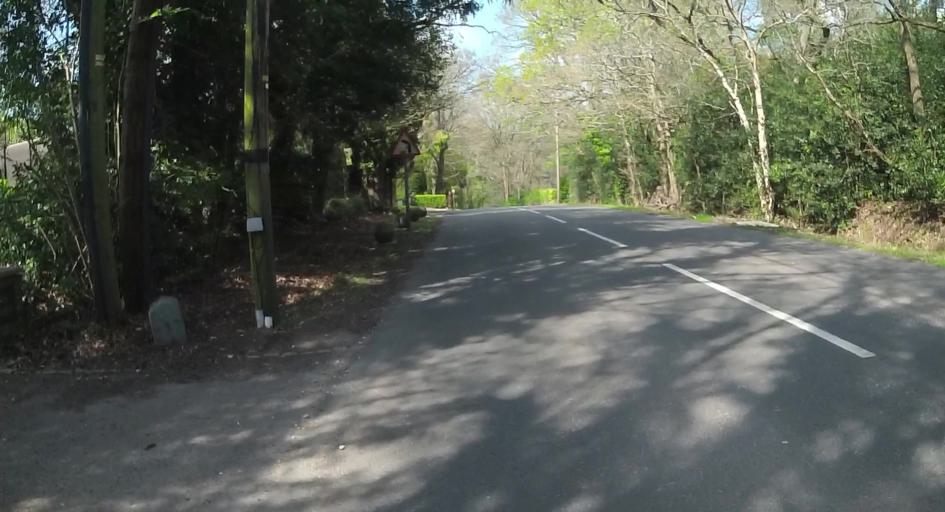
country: GB
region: England
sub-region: Hampshire
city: Tadley
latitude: 51.3629
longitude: -1.1132
